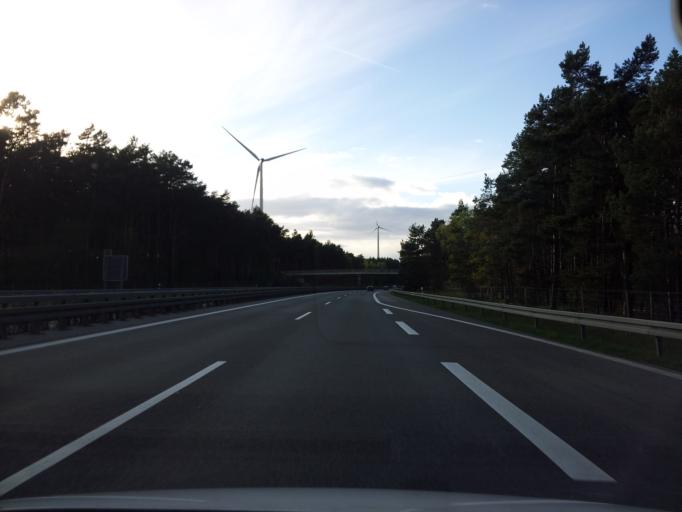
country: DE
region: Brandenburg
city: Vetschau
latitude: 51.7564
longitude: 14.1224
